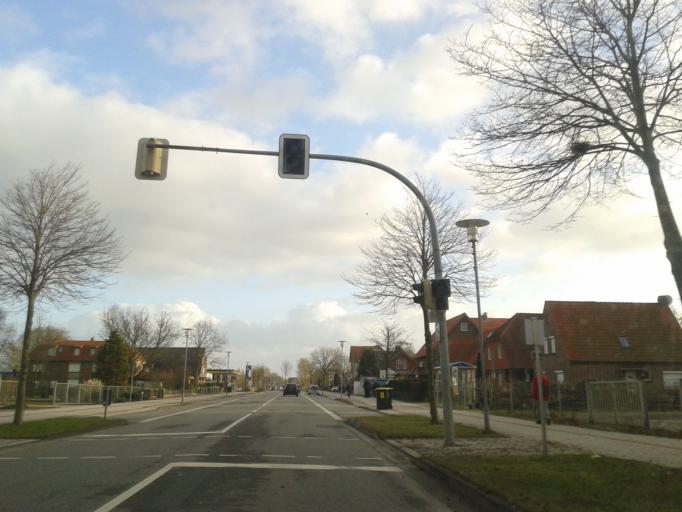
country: DE
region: Lower Saxony
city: Norddeich
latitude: 53.6149
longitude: 7.1643
